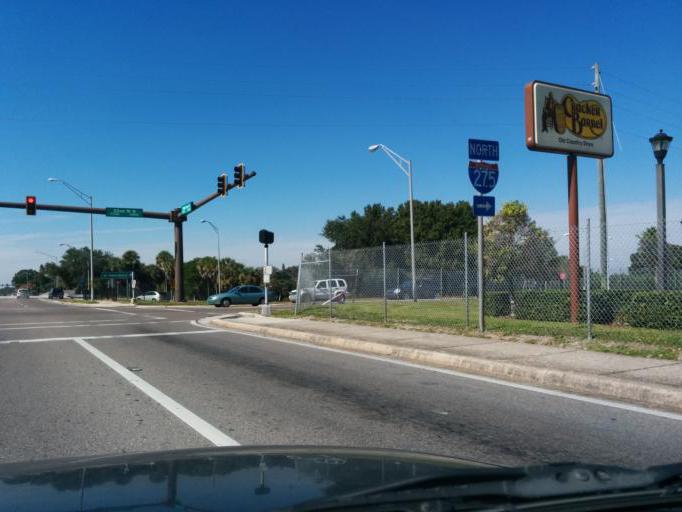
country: US
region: Florida
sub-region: Pinellas County
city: Lealman
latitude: 27.8212
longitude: -82.6628
